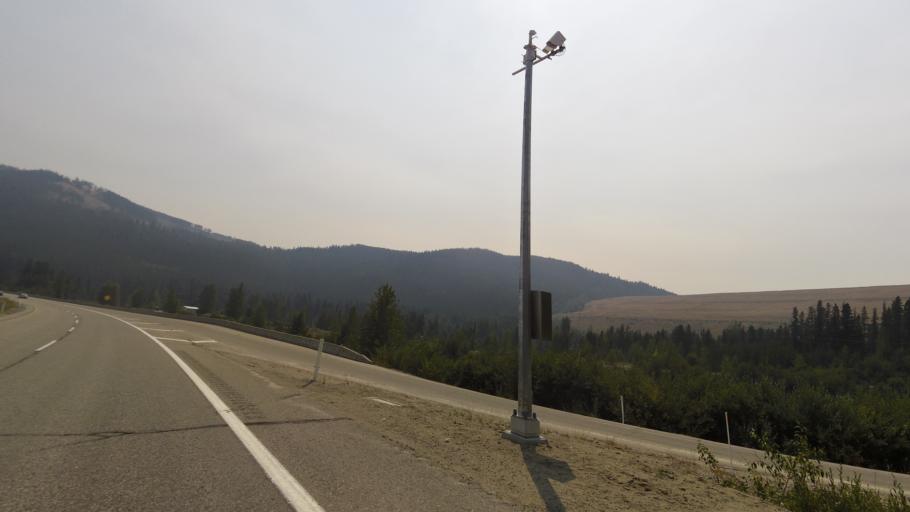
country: CA
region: British Columbia
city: Peachland
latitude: 49.8697
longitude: -119.9367
